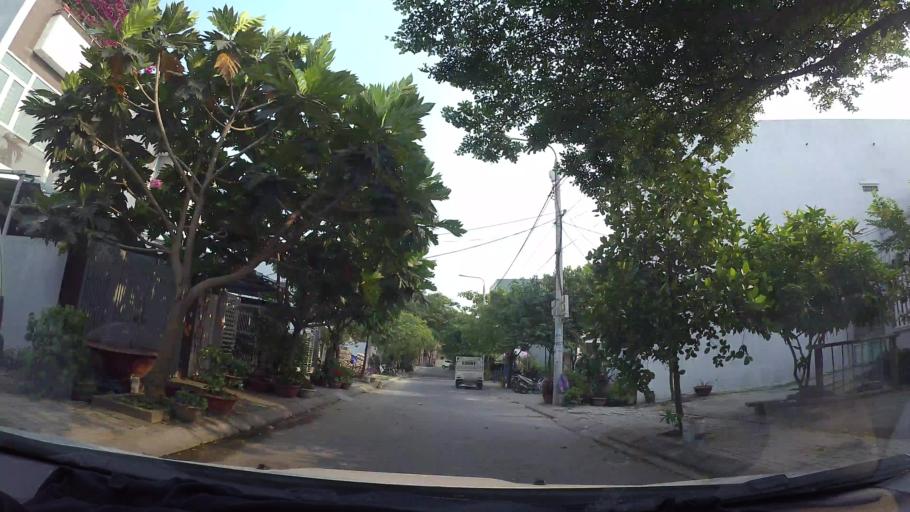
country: VN
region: Da Nang
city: Cam Le
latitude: 16.0207
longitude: 108.2060
